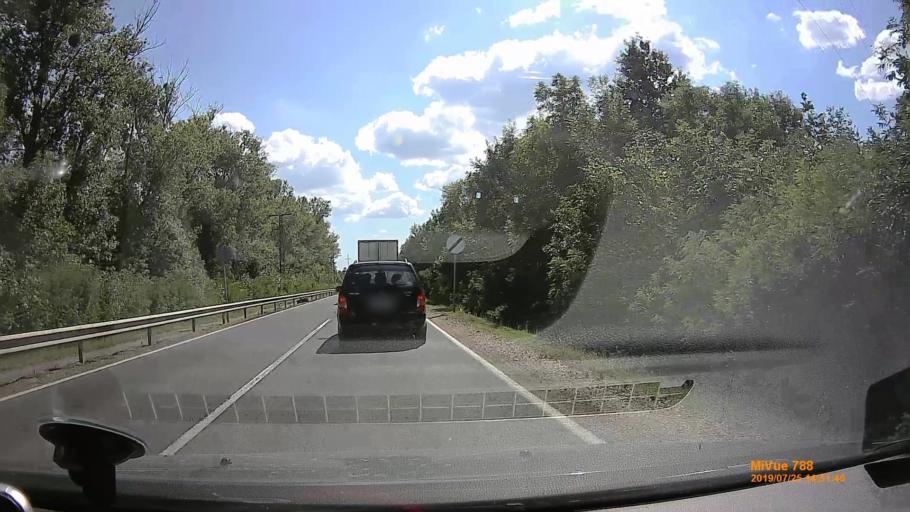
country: HU
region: Borsod-Abauj-Zemplen
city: Szikszo
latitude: 48.2119
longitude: 20.9404
